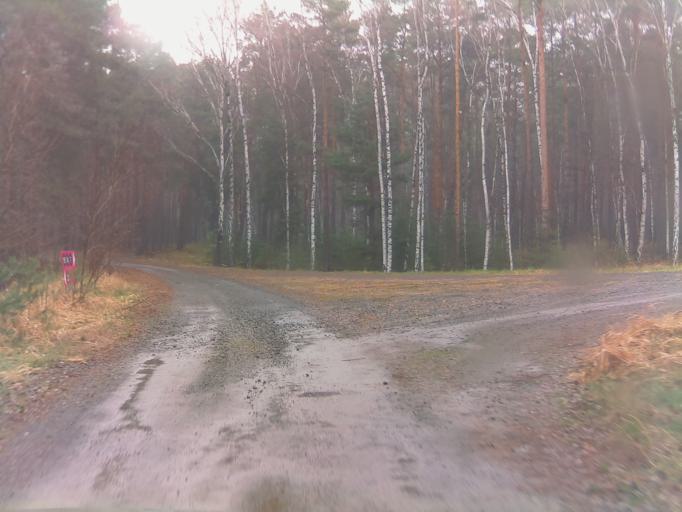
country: DE
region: Brandenburg
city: Jamlitz
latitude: 52.0563
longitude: 14.3584
